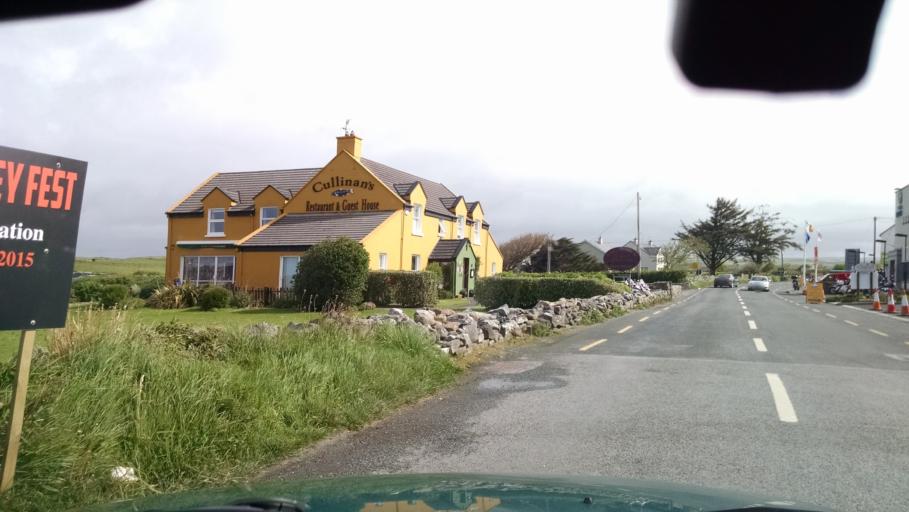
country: IE
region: Connaught
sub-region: County Galway
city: Bearna
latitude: 53.0160
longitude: -9.3775
